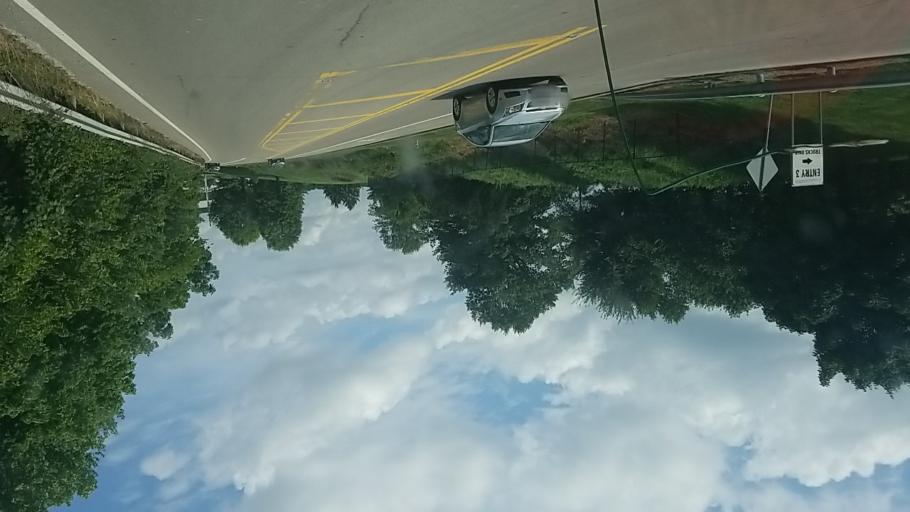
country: US
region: Ohio
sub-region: Franklin County
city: Gahanna
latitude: 40.0545
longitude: -82.8909
